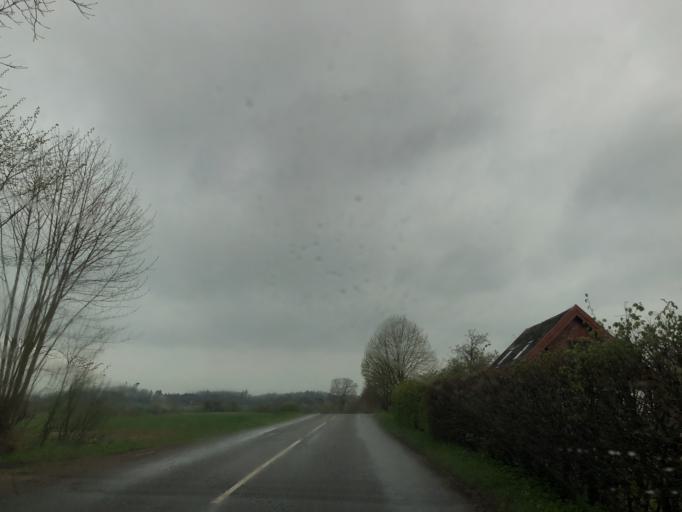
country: DK
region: Zealand
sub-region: Lejre Kommune
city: Kirke Hvalso
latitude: 55.5283
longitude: 11.8572
